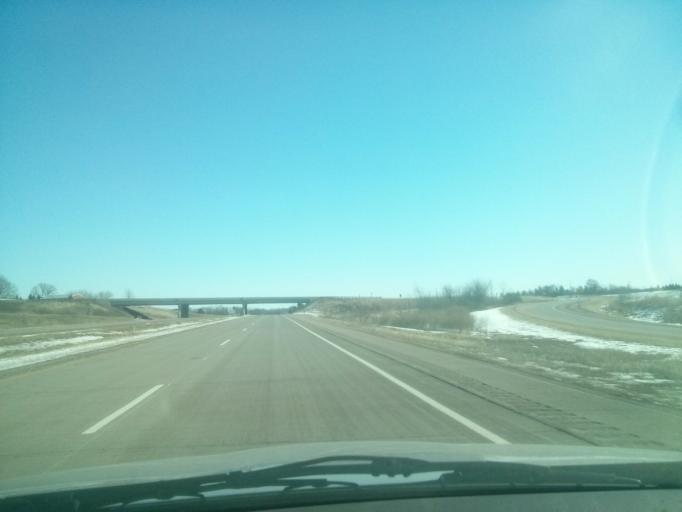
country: US
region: Wisconsin
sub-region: Saint Croix County
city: Somerset
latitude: 45.1196
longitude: -92.6586
